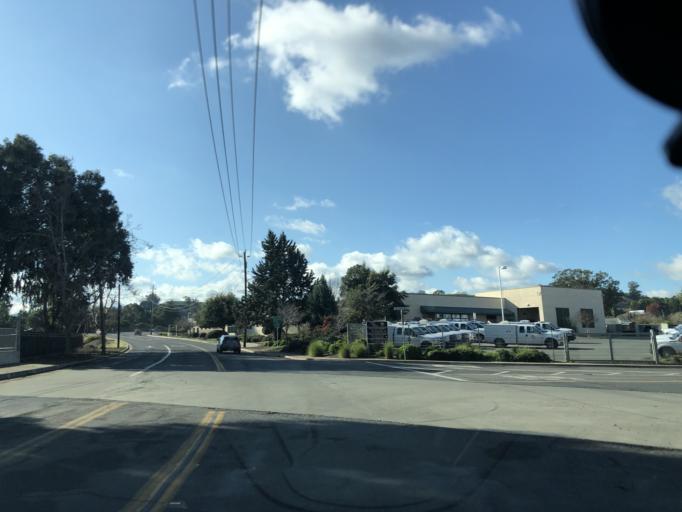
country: US
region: California
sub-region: Contra Costa County
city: Pacheco
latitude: 38.0001
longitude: -122.0698
